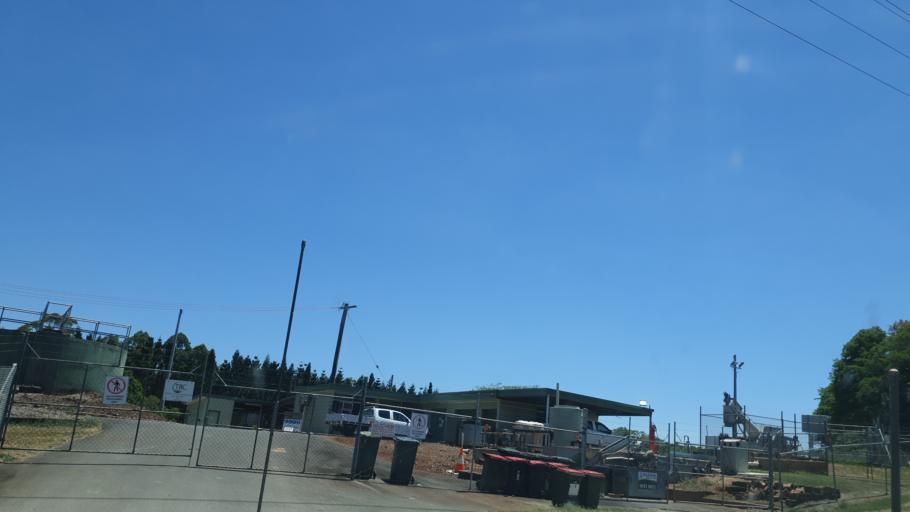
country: AU
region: Queensland
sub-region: Tablelands
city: Atherton
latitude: -17.2548
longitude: 145.4800
